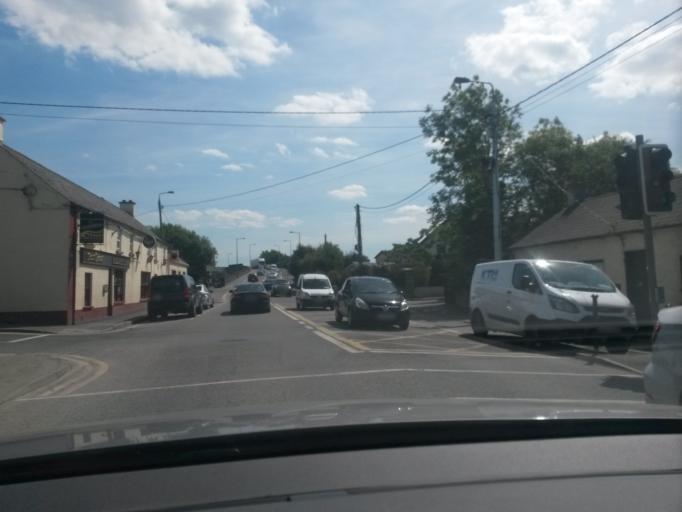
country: IE
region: Leinster
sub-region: Kildare
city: Sallins
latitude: 53.2486
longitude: -6.6654
